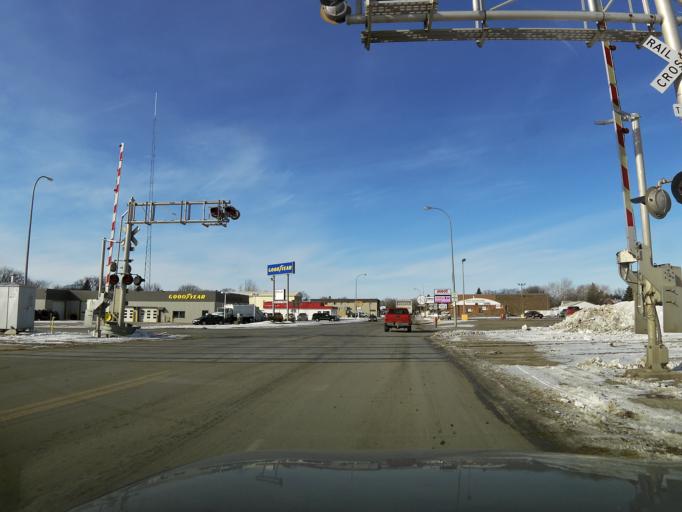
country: US
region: North Dakota
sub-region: Walsh County
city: Grafton
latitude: 48.4125
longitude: -97.4071
